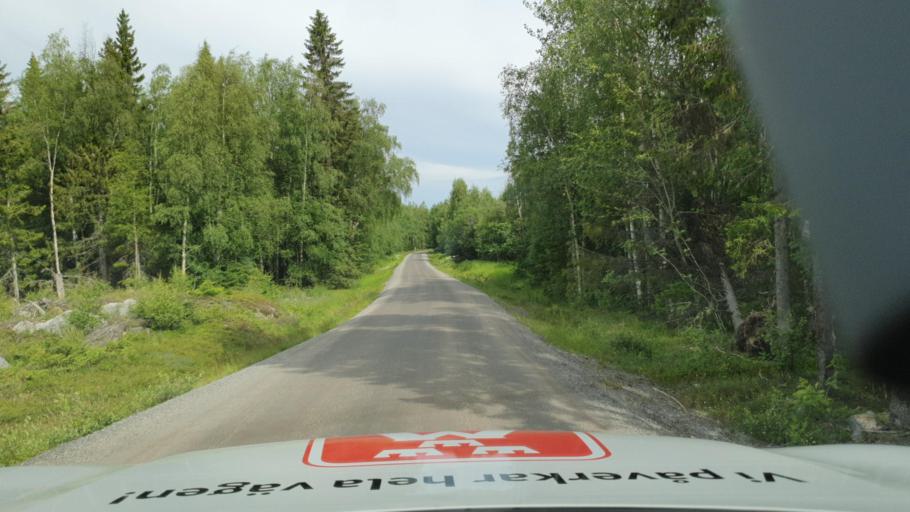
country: SE
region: Vaesterbotten
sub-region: Robertsfors Kommun
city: Robertsfors
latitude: 64.0331
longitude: 20.8849
